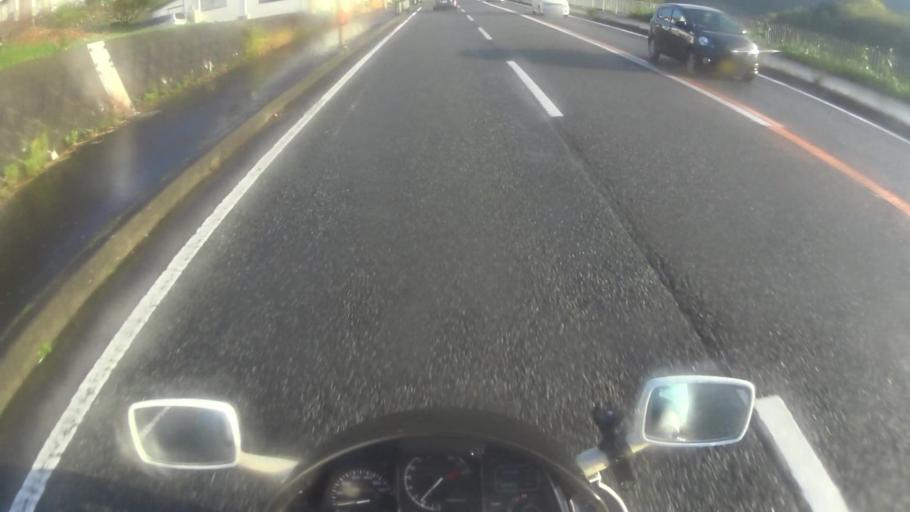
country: JP
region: Kyoto
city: Ayabe
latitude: 35.2245
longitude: 135.2252
